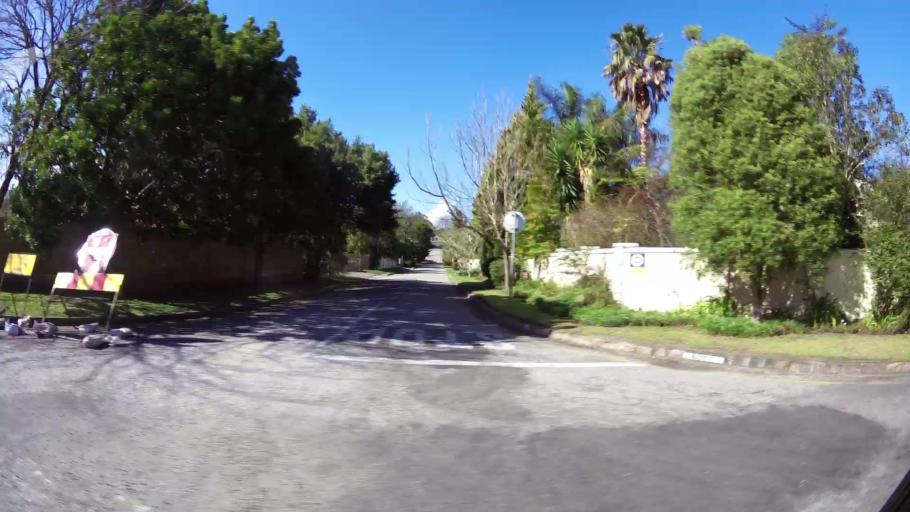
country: ZA
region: Western Cape
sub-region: Eden District Municipality
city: George
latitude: -33.9490
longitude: 22.4572
